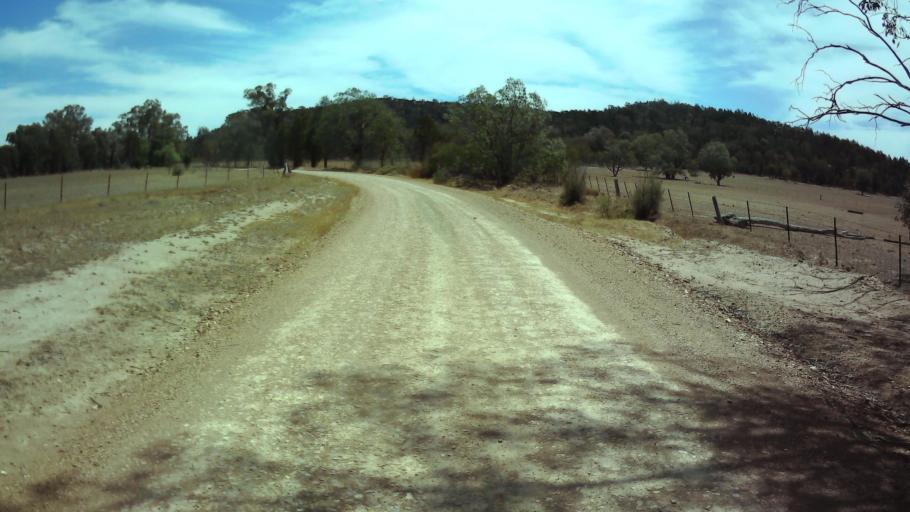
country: AU
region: New South Wales
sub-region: Weddin
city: Grenfell
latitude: -33.7470
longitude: 148.1989
